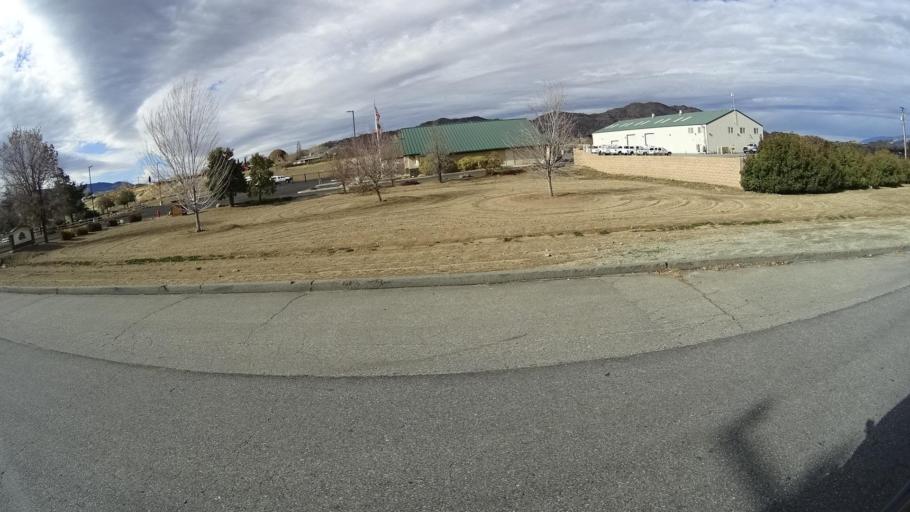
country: US
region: California
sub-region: Kern County
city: Golden Hills
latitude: 35.1310
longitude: -118.4768
